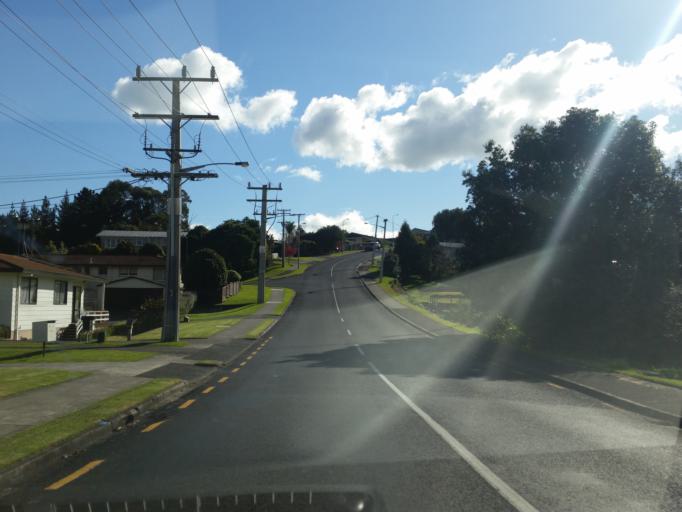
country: NZ
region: Bay of Plenty
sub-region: Tauranga City
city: Tauranga
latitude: -37.6850
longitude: 176.1279
